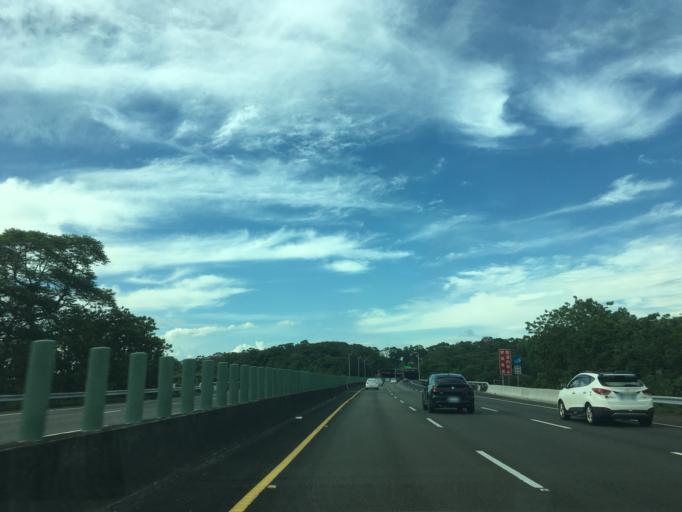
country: TW
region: Taiwan
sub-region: Chiayi
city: Jiayi Shi
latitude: 23.5723
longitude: 120.5061
